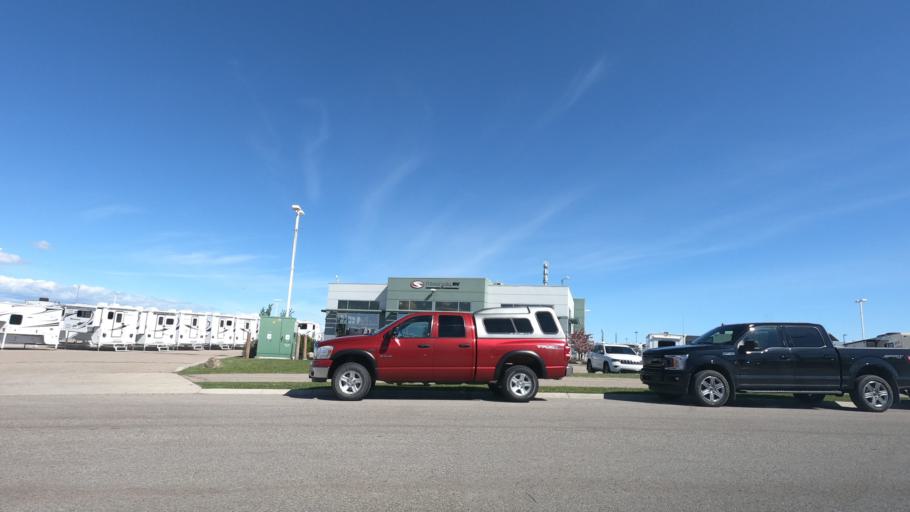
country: CA
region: Alberta
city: Airdrie
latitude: 51.2616
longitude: -113.9977
